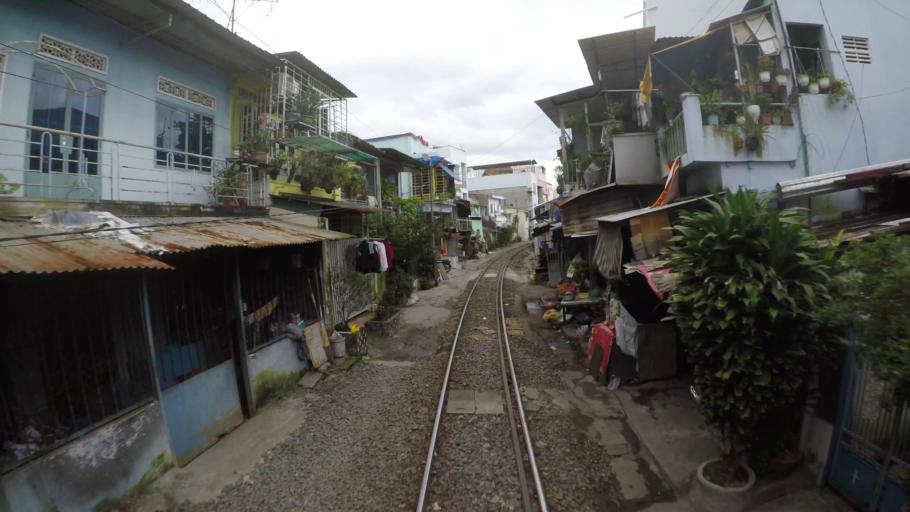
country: VN
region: Khanh Hoa
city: Nha Trang
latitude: 12.2459
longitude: 109.1843
